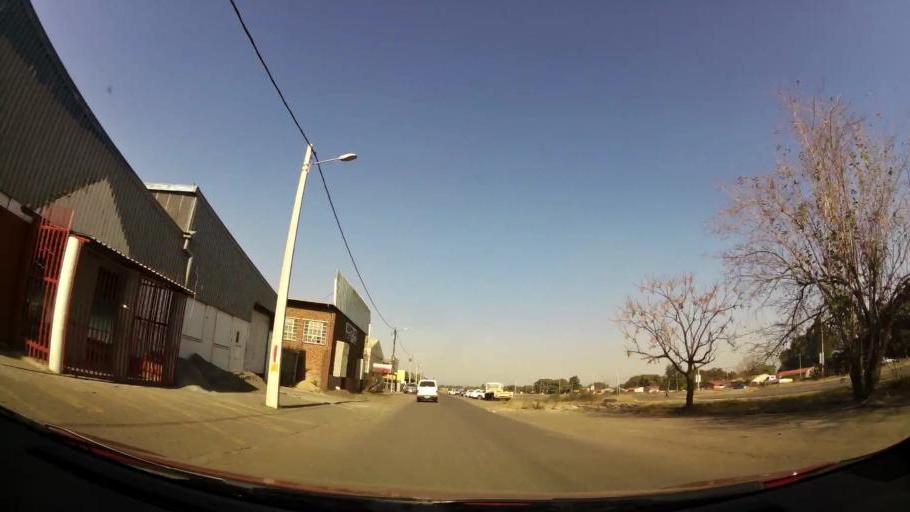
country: ZA
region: North-West
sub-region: Bojanala Platinum District Municipality
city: Rustenburg
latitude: -25.6440
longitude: 27.2319
